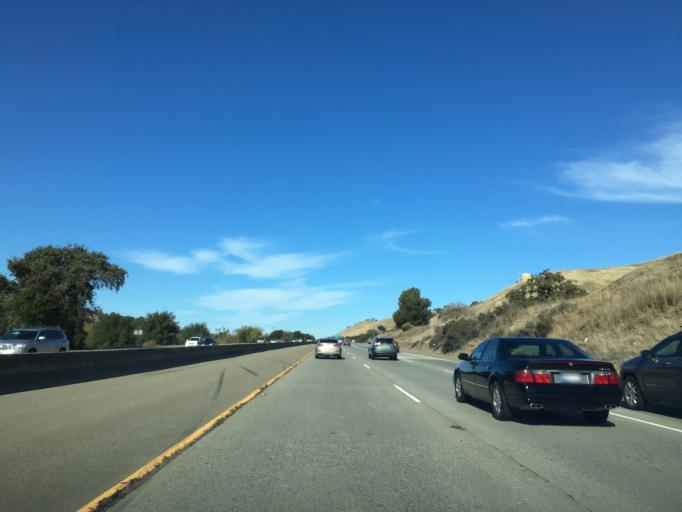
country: US
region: California
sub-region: Alameda County
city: Pleasanton
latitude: 37.6064
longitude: -121.8728
